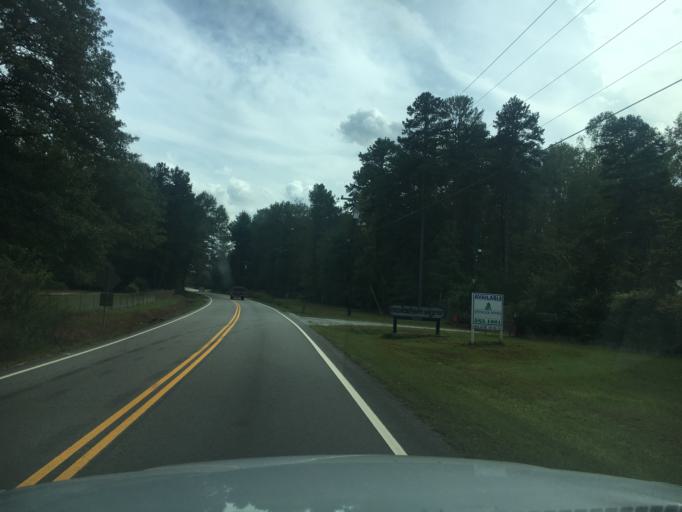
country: US
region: South Carolina
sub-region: Spartanburg County
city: Wellford
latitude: 34.9235
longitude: -82.0626
